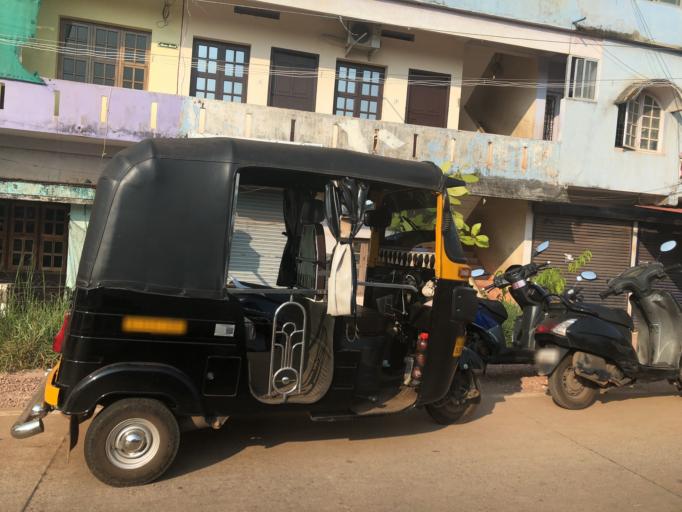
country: IN
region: Karnataka
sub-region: Dakshina Kannada
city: Ullal
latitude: 12.8166
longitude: 74.8473
